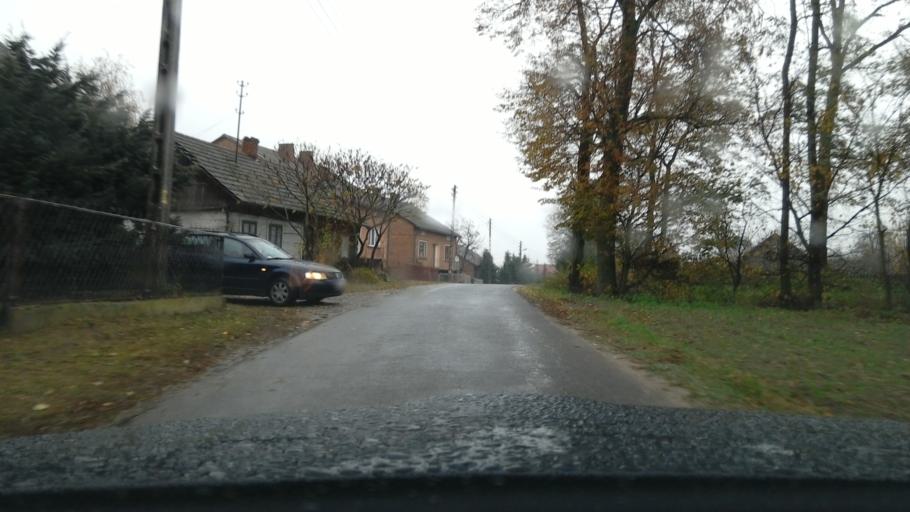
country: PL
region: Lodz Voivodeship
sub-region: Powiat skierniewicki
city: Godzianow
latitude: 51.9010
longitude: 20.0583
